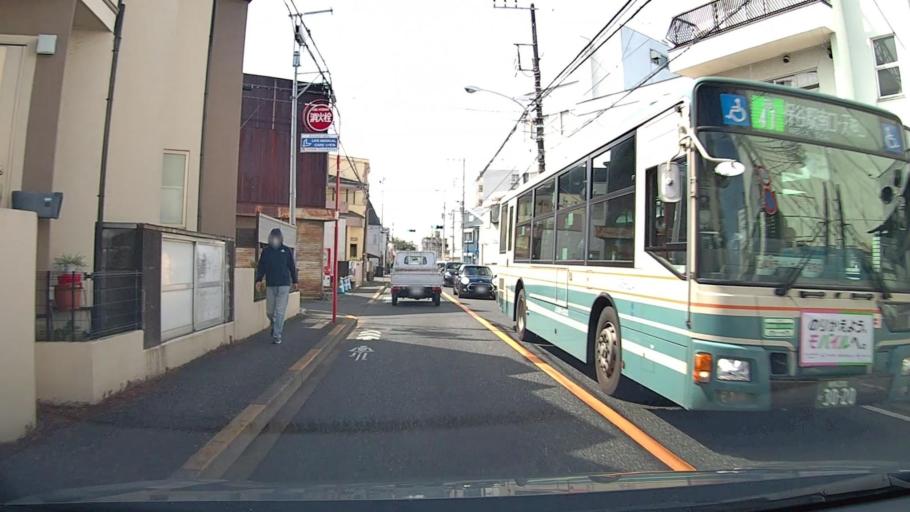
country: JP
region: Tokyo
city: Nishi-Tokyo-shi
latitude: 35.7352
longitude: 139.5515
